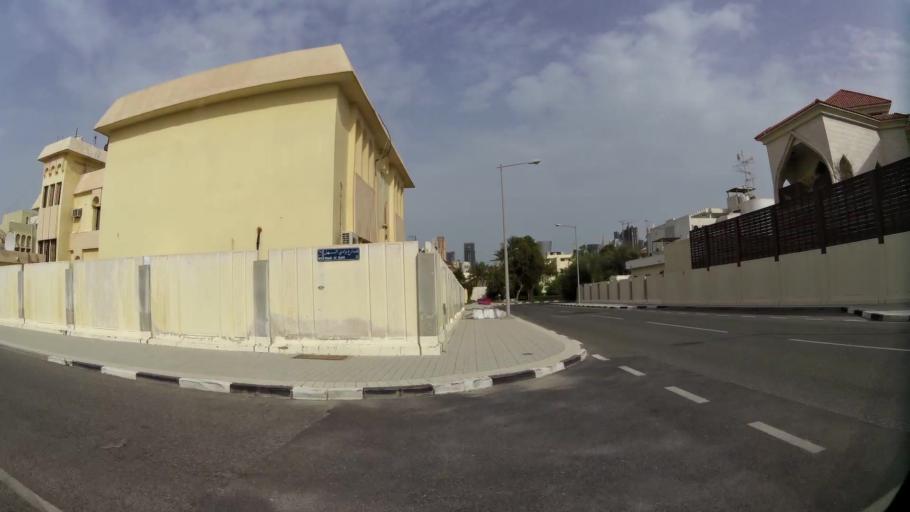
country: QA
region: Baladiyat ad Dawhah
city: Doha
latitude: 25.3248
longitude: 51.5080
